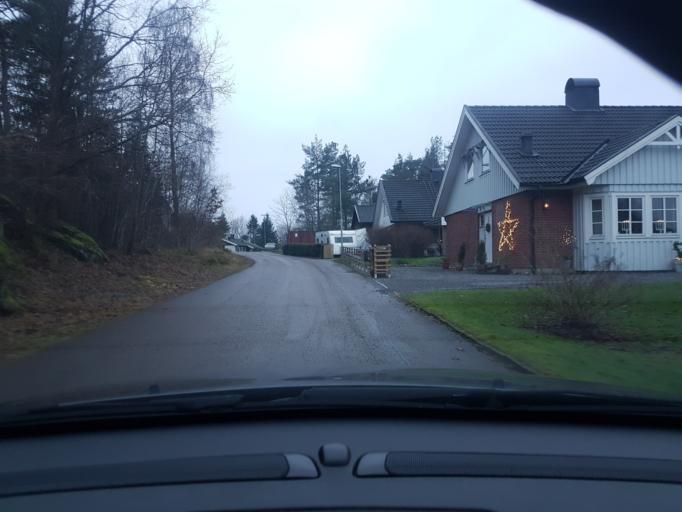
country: SE
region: Vaestra Goetaland
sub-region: Ale Kommun
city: Alvangen
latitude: 57.9529
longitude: 12.1340
